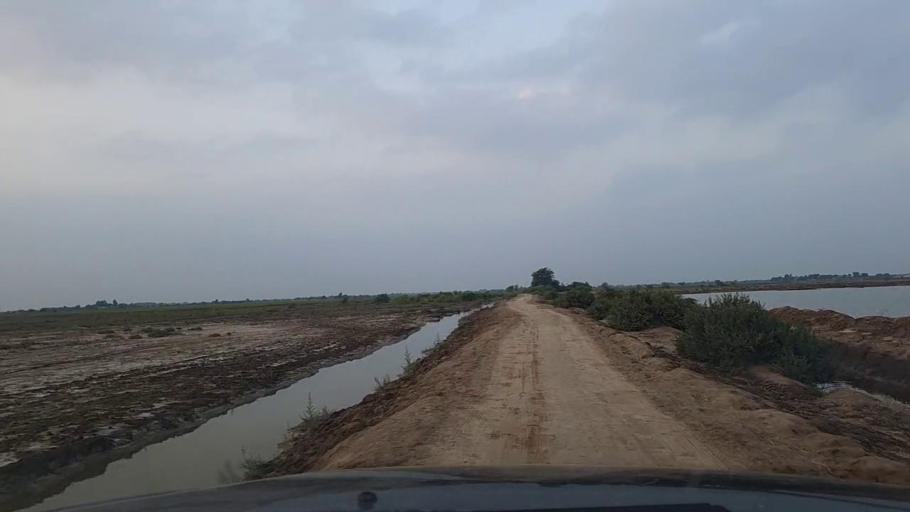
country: PK
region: Sindh
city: Jati
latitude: 24.4955
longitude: 68.3910
